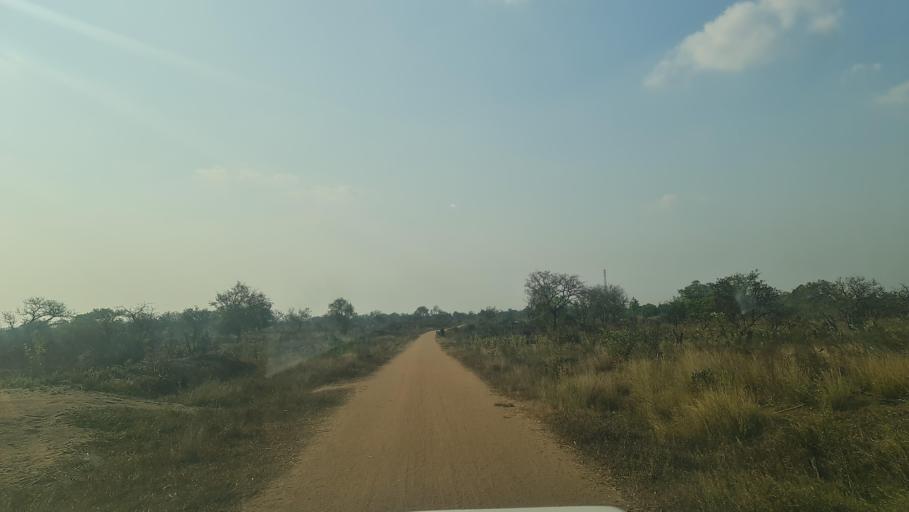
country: MZ
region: Zambezia
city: Quelimane
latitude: -18.1511
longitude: 35.9889
